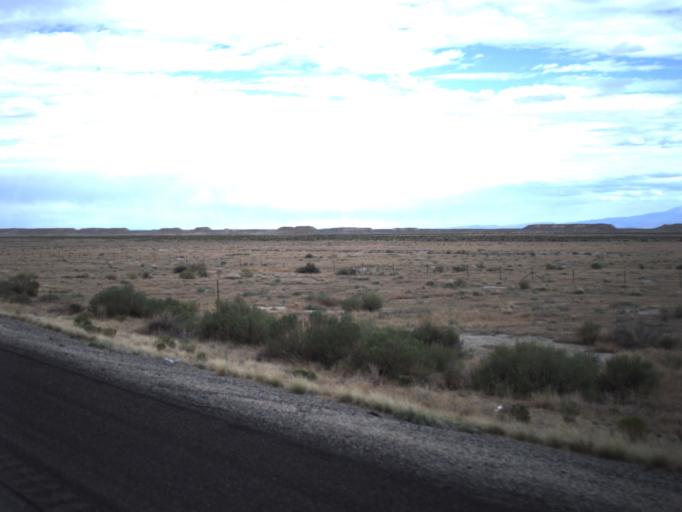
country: US
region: Utah
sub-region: Grand County
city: Moab
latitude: 38.9490
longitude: -109.7797
